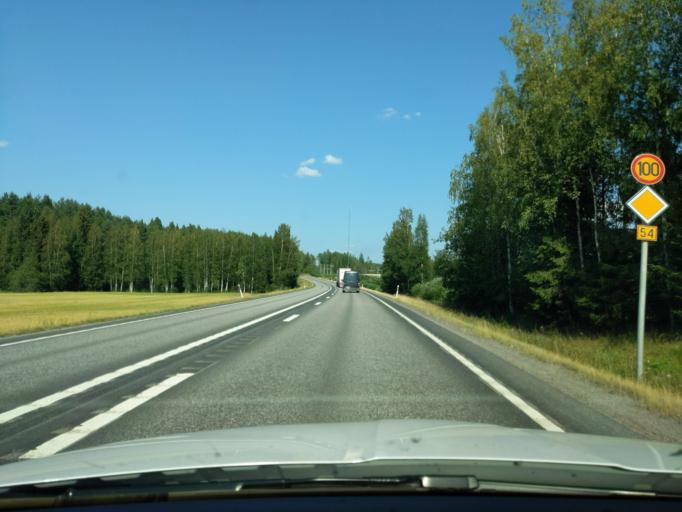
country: FI
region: Paijanne Tavastia
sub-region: Lahti
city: Jaervelae
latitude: 60.9105
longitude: 25.3409
